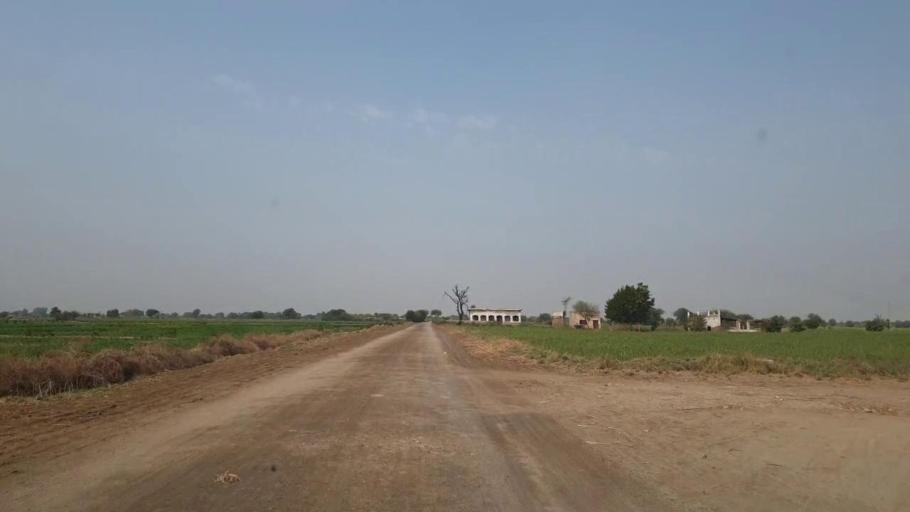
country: PK
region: Sindh
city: Mirpur Khas
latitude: 25.5641
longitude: 69.1524
